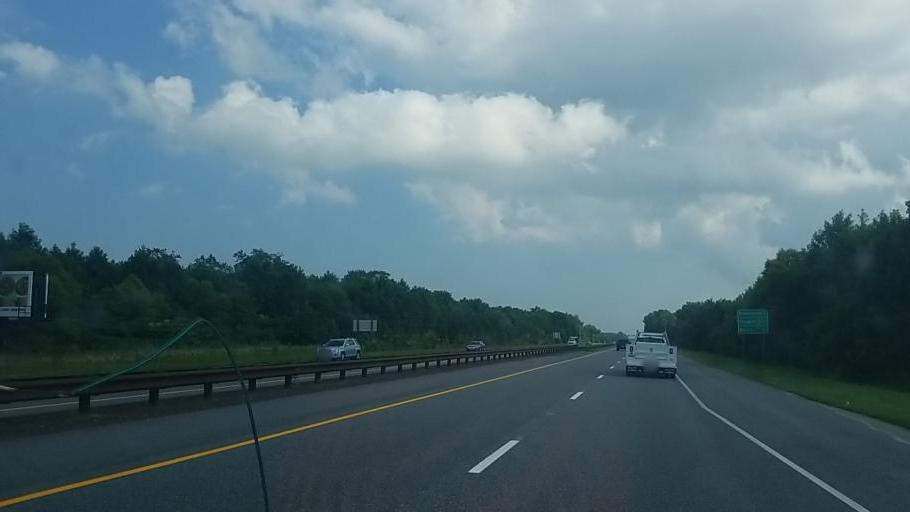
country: US
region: Delaware
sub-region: Sussex County
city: Selbyville
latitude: 38.4396
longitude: -75.2260
